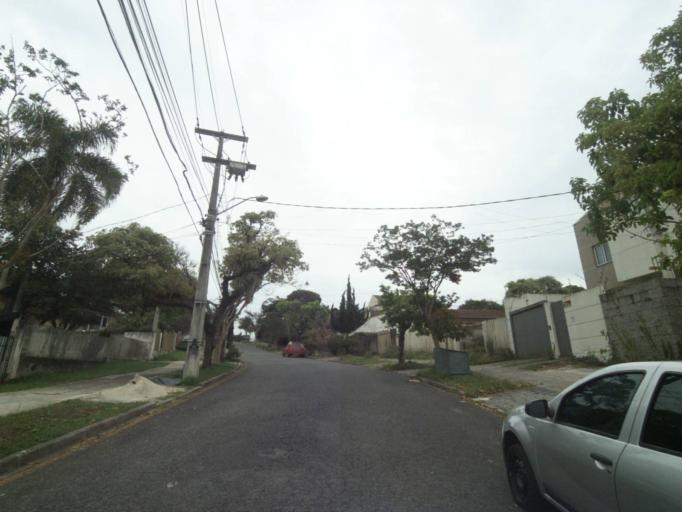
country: BR
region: Parana
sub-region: Curitiba
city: Curitiba
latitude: -25.4035
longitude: -49.2757
